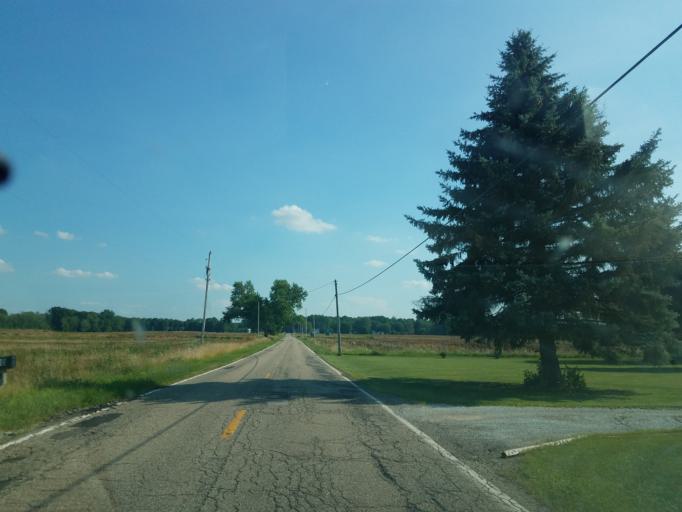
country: US
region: Ohio
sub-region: Stark County
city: Uniontown
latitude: 40.9578
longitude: -81.4212
